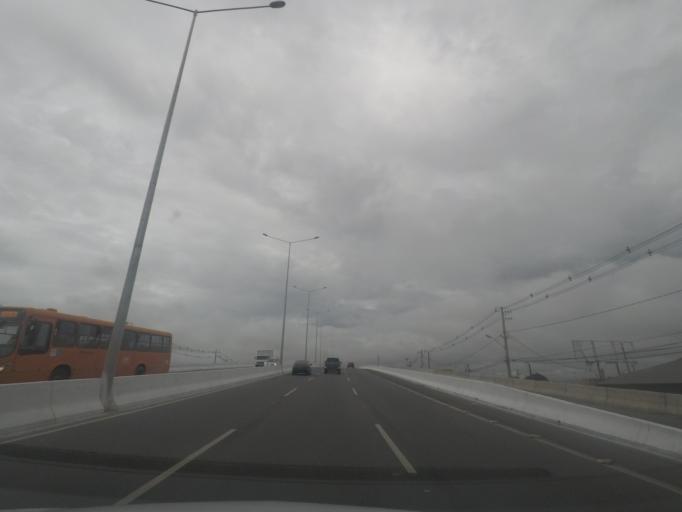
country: BR
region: Parana
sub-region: Pinhais
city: Pinhais
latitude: -25.4387
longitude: -49.1604
